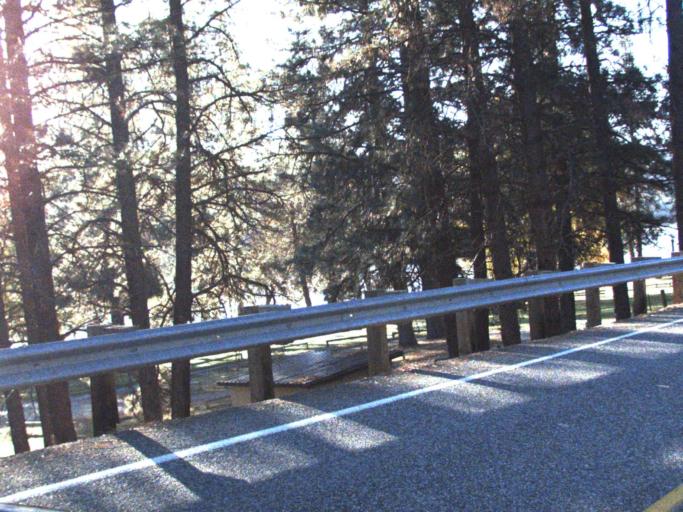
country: US
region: Washington
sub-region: Okanogan County
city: Coulee Dam
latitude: 48.0413
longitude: -118.6705
